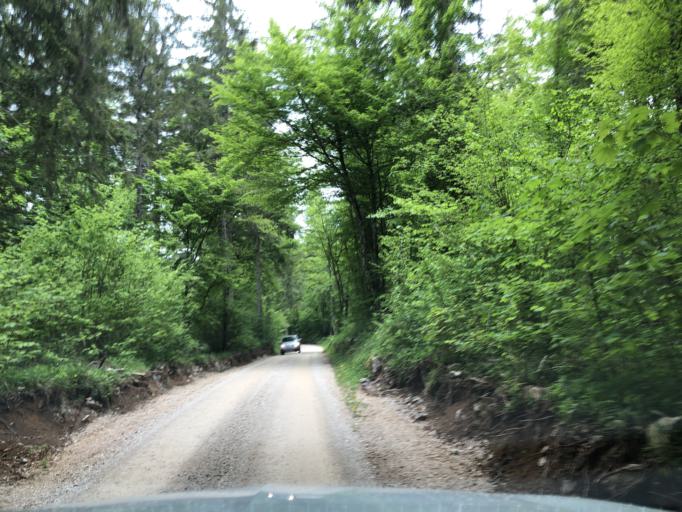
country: SI
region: Bloke
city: Nova Vas
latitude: 45.7490
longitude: 14.4659
